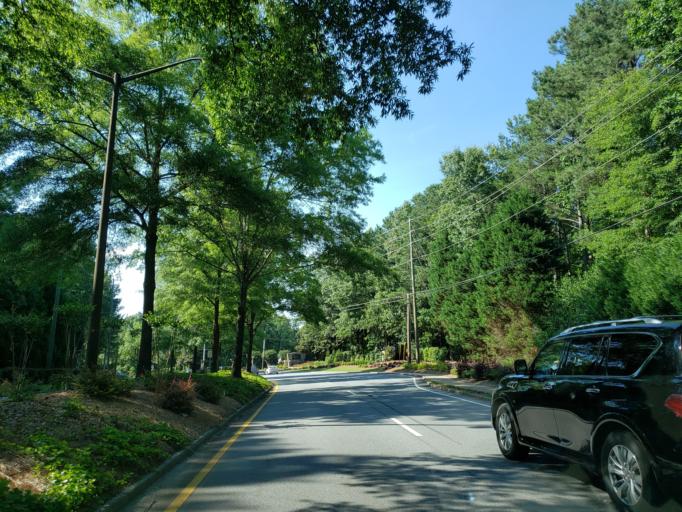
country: US
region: Georgia
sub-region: Cherokee County
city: Woodstock
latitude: 34.1292
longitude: -84.5600
